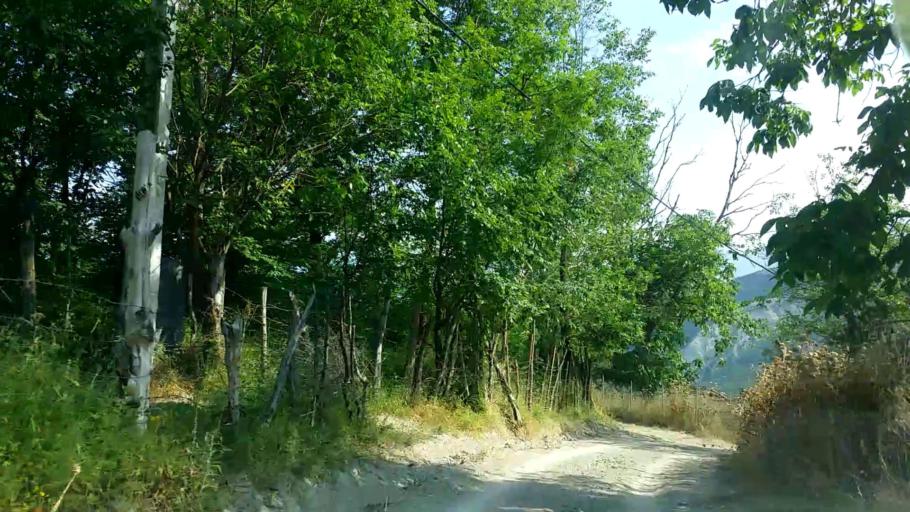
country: IR
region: Mazandaran
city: Chalus
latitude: 36.5470
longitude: 51.2945
